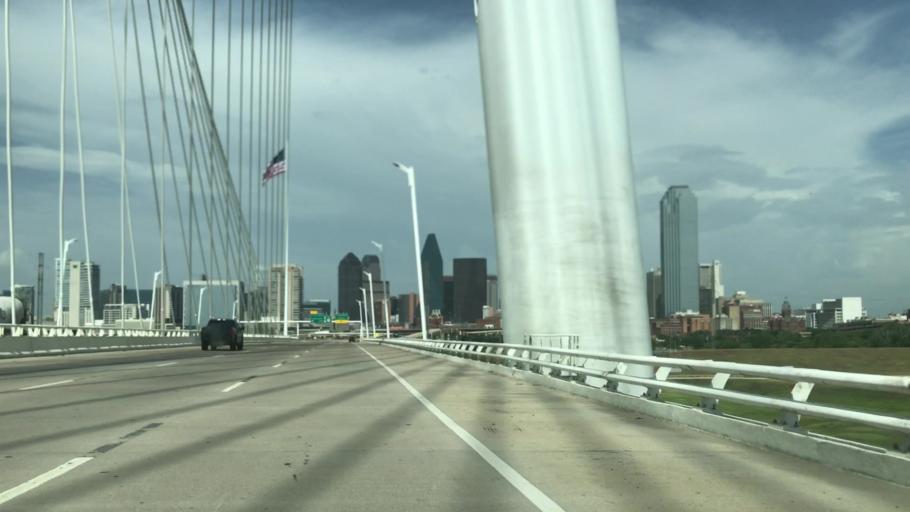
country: US
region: Texas
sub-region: Dallas County
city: Dallas
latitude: 32.7799
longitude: -96.8223
